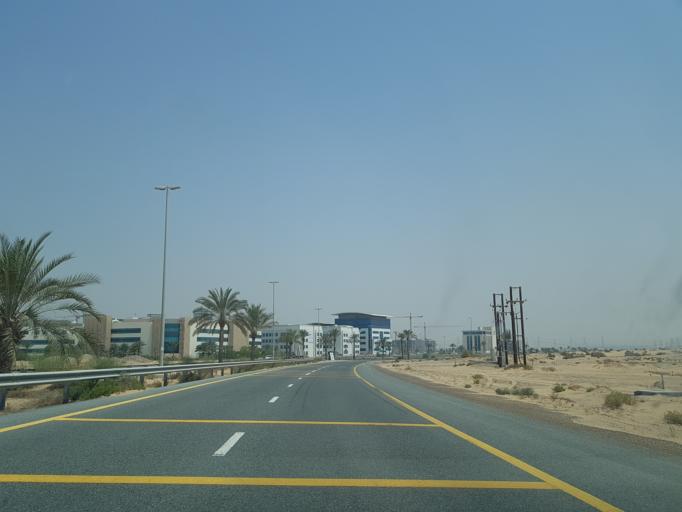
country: AE
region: Ash Shariqah
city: Sharjah
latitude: 25.1211
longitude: 55.4271
